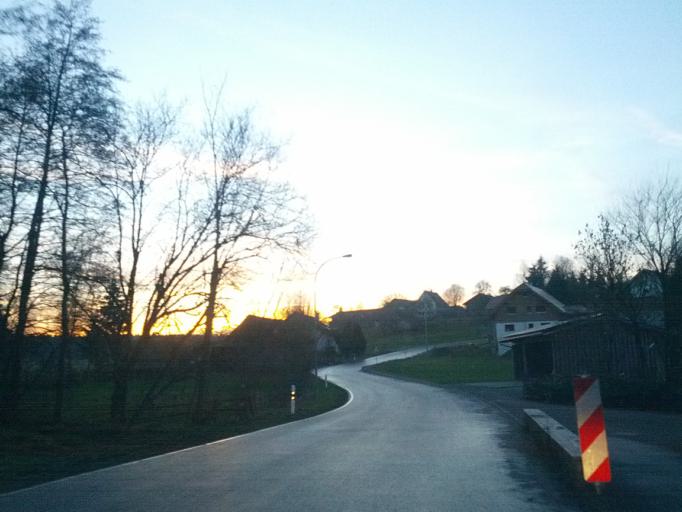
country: DE
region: Baden-Wuerttemberg
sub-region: Tuebingen Region
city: Aitrach
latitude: 47.9394
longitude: 10.0251
